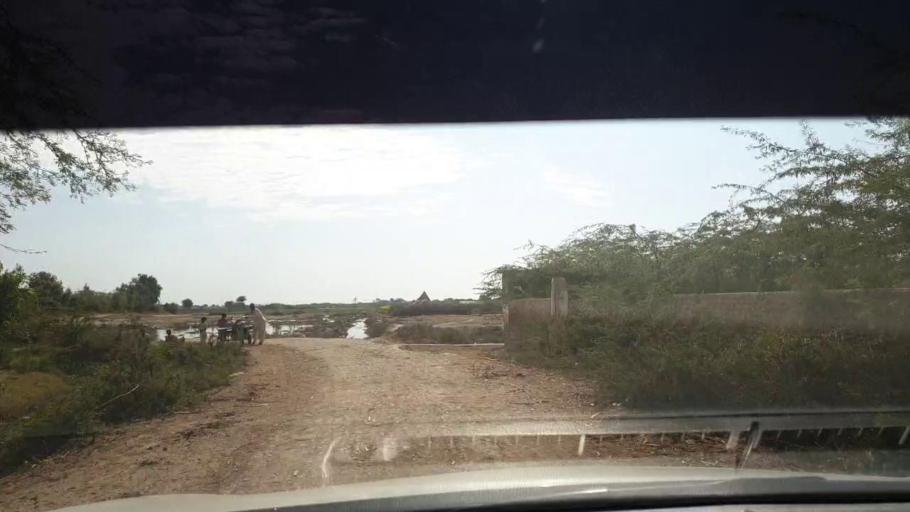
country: PK
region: Sindh
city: Berani
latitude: 25.8427
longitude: 68.8571
